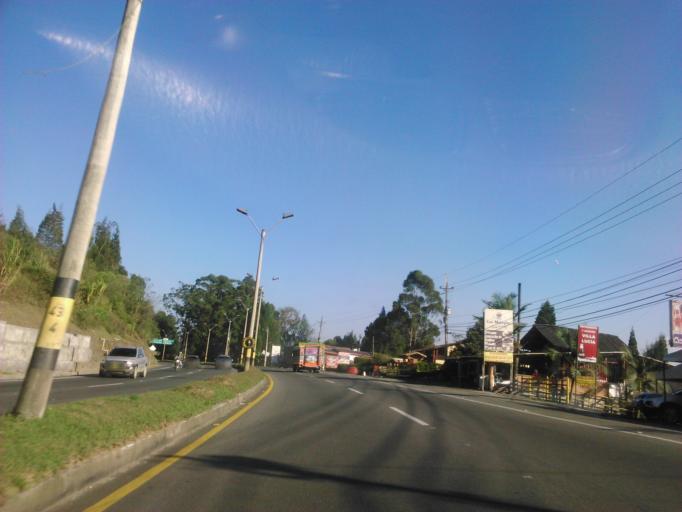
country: CO
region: Antioquia
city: Guarne
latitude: 6.2548
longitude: -75.4332
